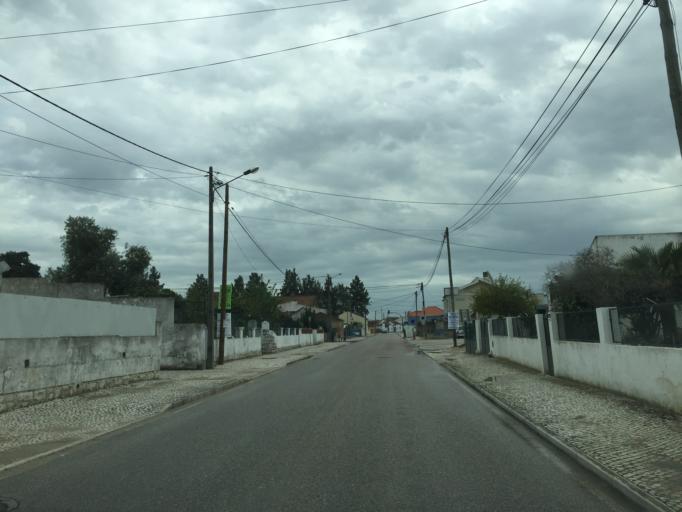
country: PT
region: Lisbon
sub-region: Azambuja
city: Aveiras de Cima
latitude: 39.1436
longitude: -8.9014
